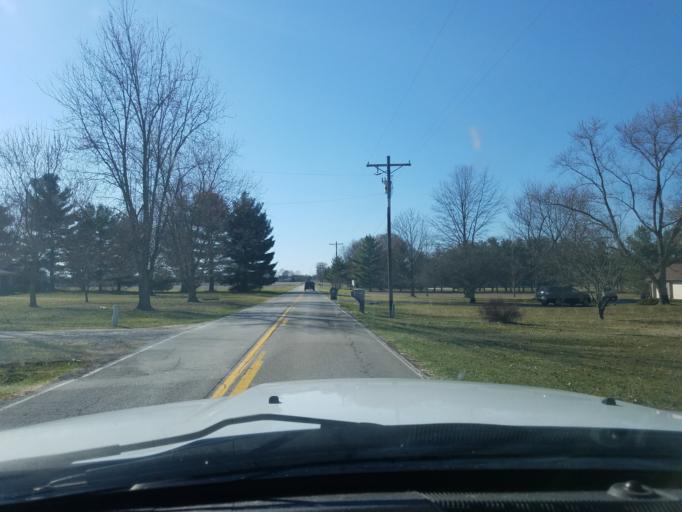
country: US
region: Indiana
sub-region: Johnson County
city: Franklin
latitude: 39.4968
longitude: -85.9963
